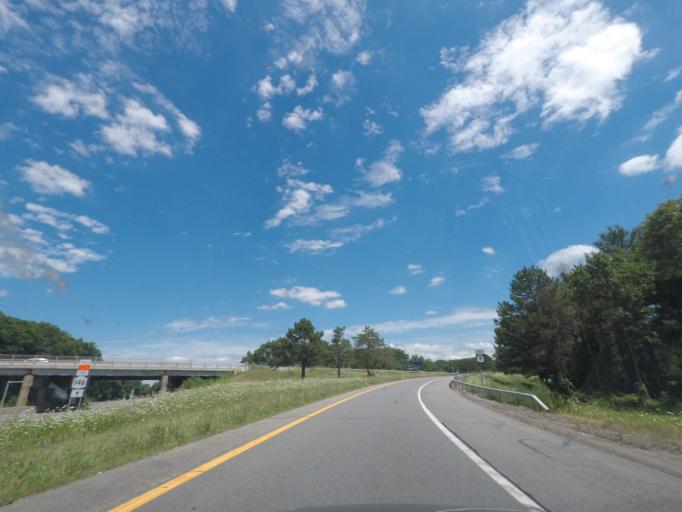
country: US
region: New York
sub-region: Schenectady County
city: Schenectady
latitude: 42.7814
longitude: -73.9230
